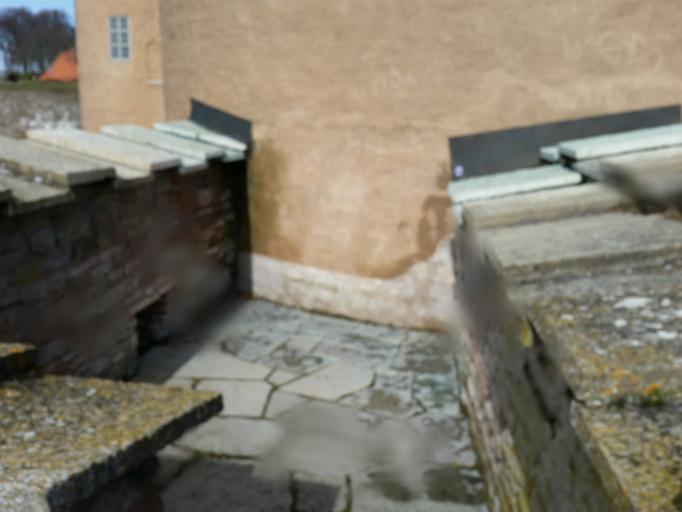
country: SE
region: Kalmar
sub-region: Kalmar Kommun
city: Kalmar
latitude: 56.6575
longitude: 16.3555
